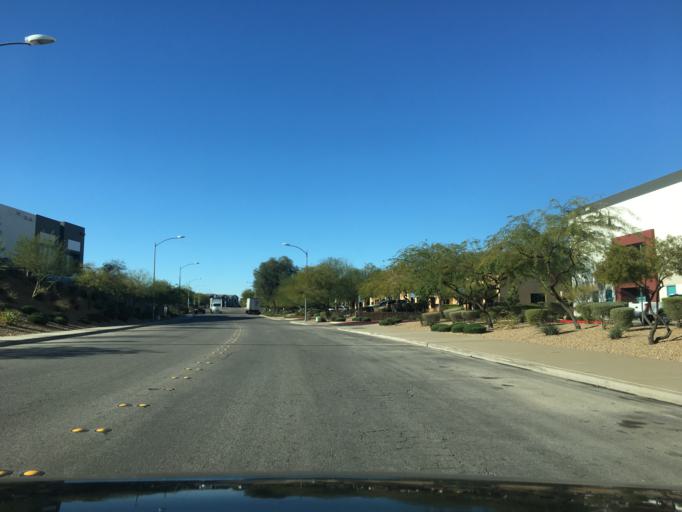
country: US
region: Nevada
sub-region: Clark County
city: Henderson
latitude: 36.0358
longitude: -115.0228
